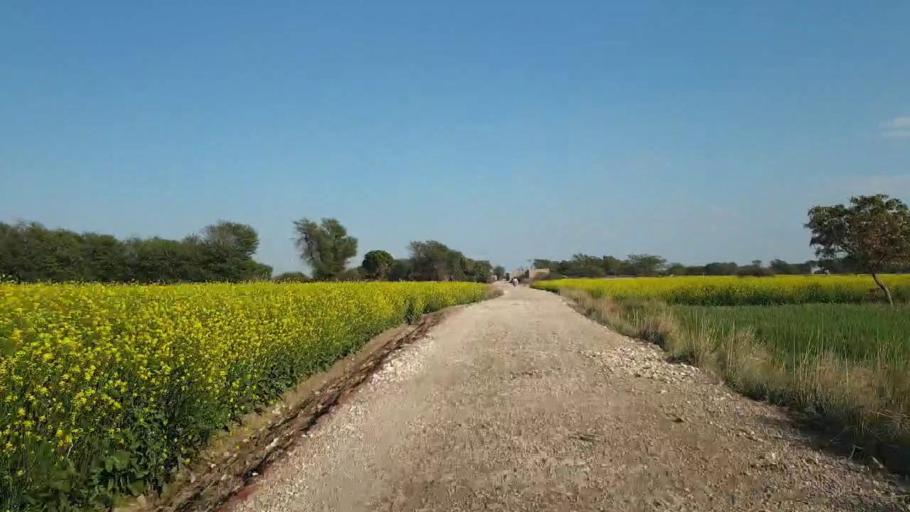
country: PK
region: Sindh
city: Shahpur Chakar
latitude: 26.1197
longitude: 68.5681
